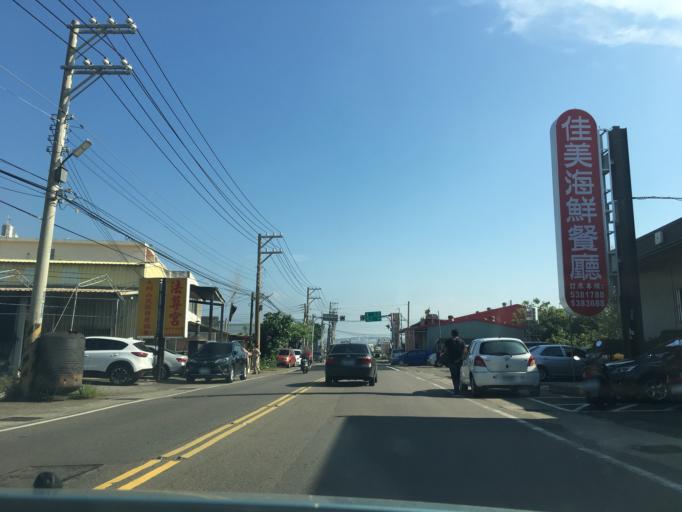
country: TW
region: Taiwan
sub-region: Hsinchu
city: Hsinchu
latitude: 24.8058
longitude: 120.9221
